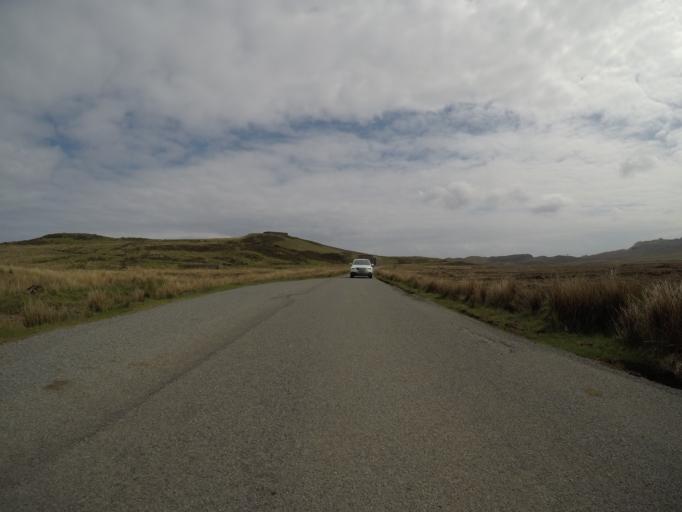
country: GB
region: Scotland
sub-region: Highland
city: Portree
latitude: 57.6810
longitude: -6.2811
